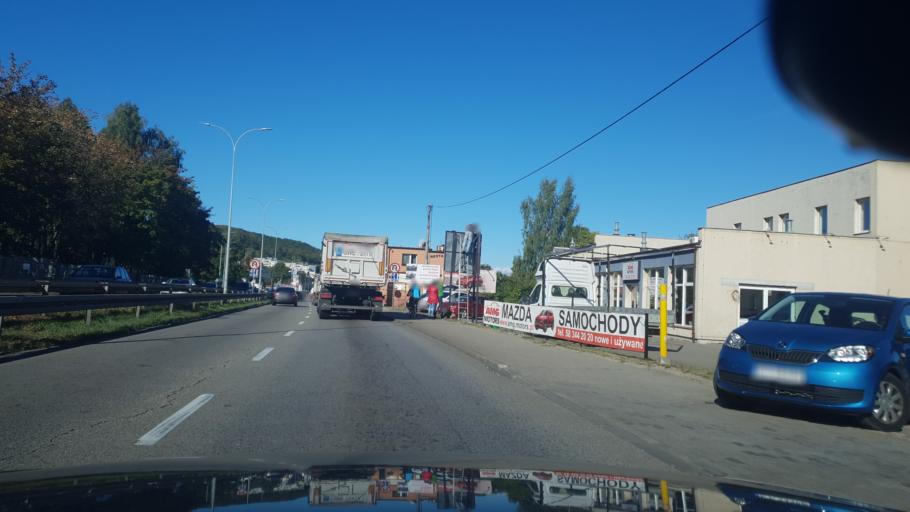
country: PL
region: Pomeranian Voivodeship
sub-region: Powiat wejherowski
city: Rumia
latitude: 54.5616
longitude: 18.3990
